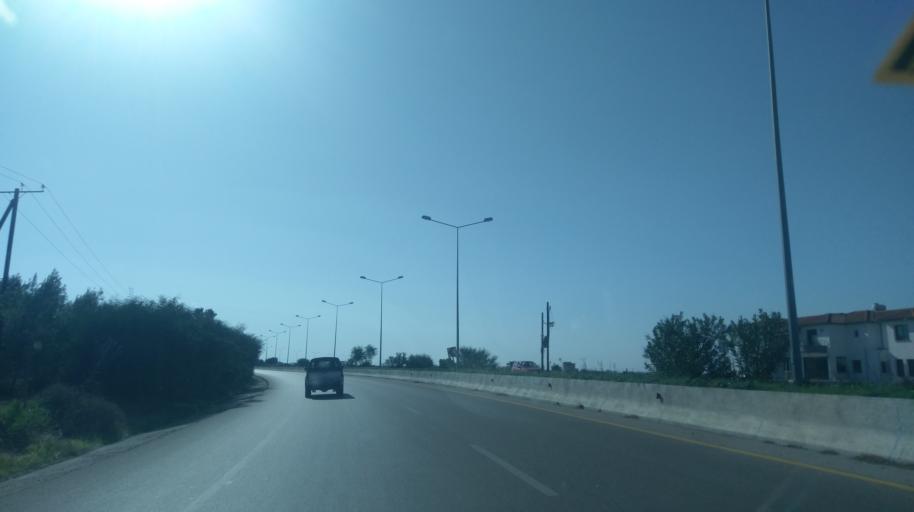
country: CY
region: Ammochostos
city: Trikomo
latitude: 35.2362
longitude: 33.8986
